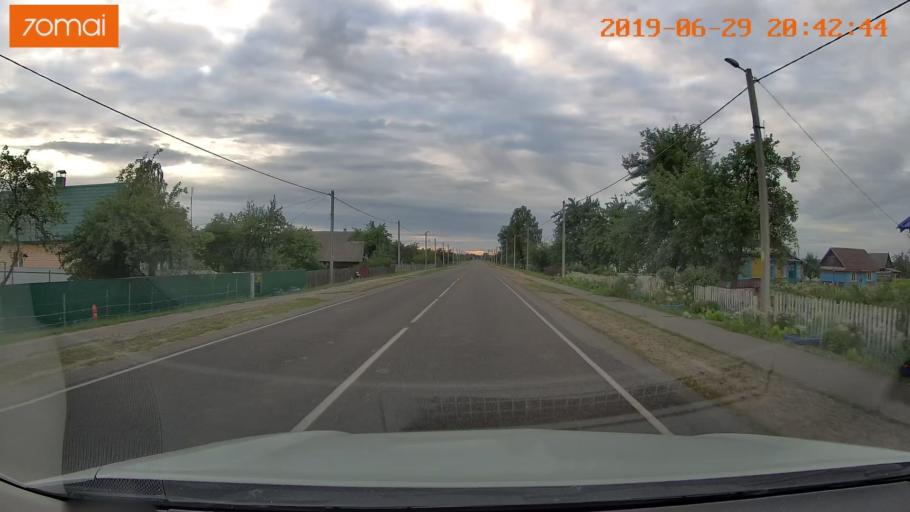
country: BY
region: Brest
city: Hantsavichy
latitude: 52.5999
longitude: 26.3228
